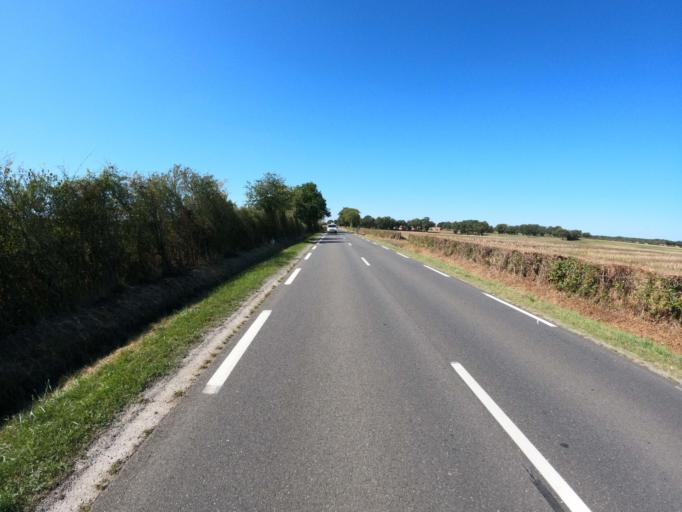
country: FR
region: Poitou-Charentes
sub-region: Departement de la Vienne
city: Montmorillon
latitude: 46.4103
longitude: 0.8094
